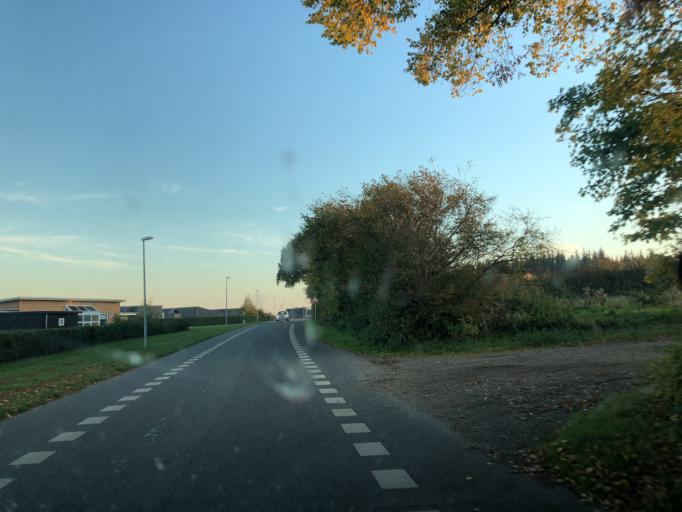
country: DK
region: South Denmark
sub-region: Vejle Kommune
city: Borkop
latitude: 55.6313
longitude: 9.6470
